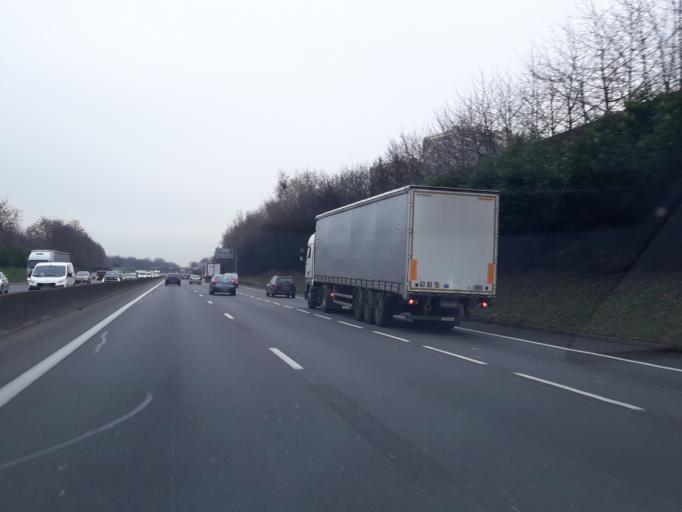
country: FR
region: Ile-de-France
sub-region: Departement de l'Essonne
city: Morsang-sur-Orge
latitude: 48.6635
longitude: 2.3665
